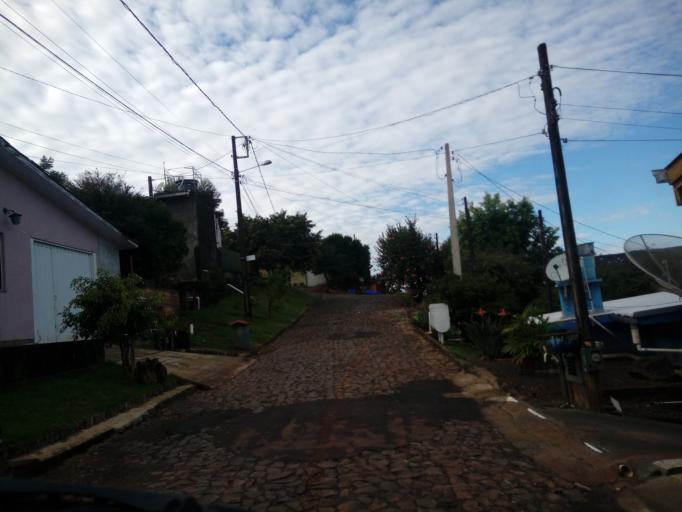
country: BR
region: Santa Catarina
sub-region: Chapeco
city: Chapeco
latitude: -27.1087
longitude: -52.6342
